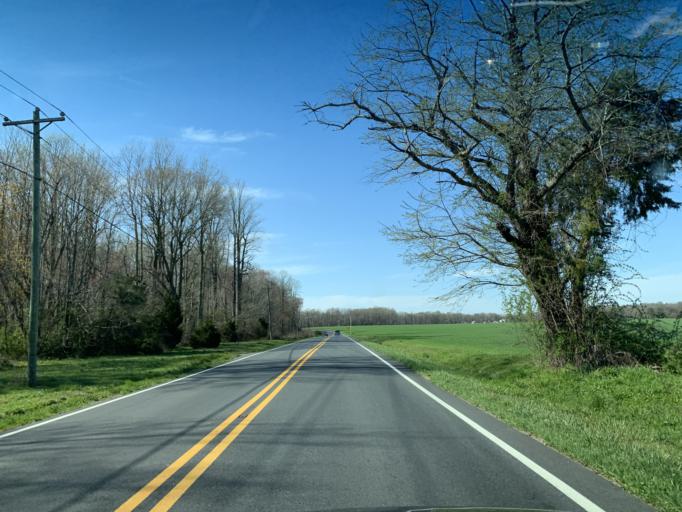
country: US
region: Delaware
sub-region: Sussex County
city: Milford
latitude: 38.9603
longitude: -75.4805
